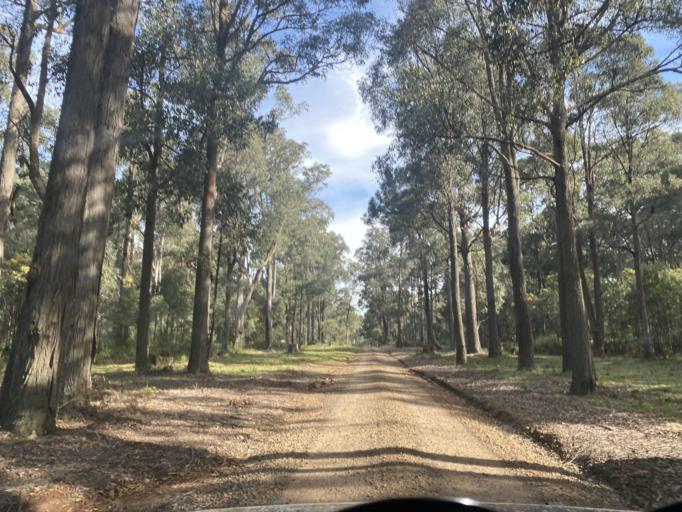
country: AU
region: Victoria
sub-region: Mansfield
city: Mansfield
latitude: -36.8439
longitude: 146.1819
